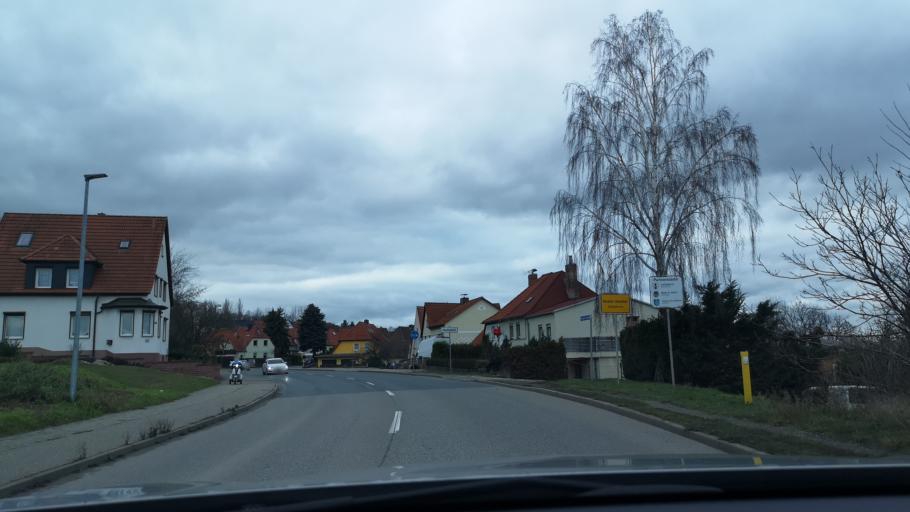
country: DE
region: Saxony-Anhalt
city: Krumpa
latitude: 51.2995
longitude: 11.8369
